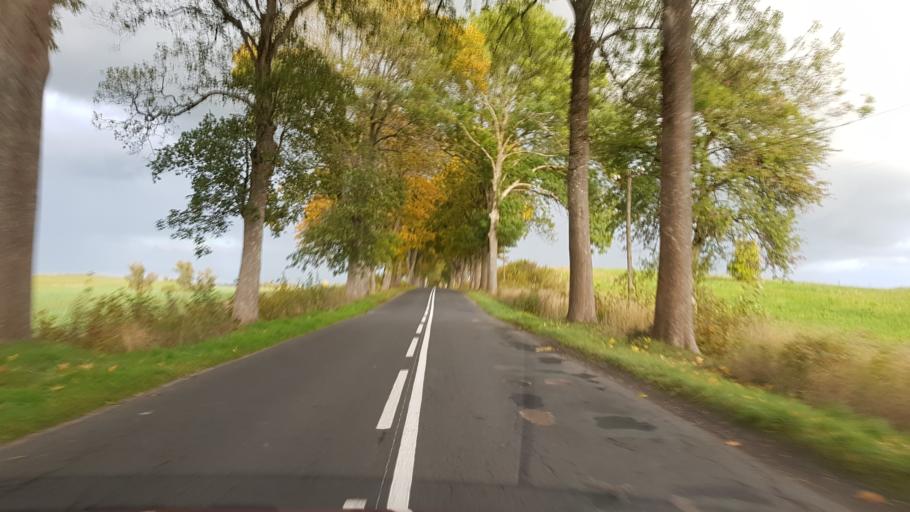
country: PL
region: West Pomeranian Voivodeship
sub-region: Powiat walecki
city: Walcz
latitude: 53.1817
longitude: 16.3639
